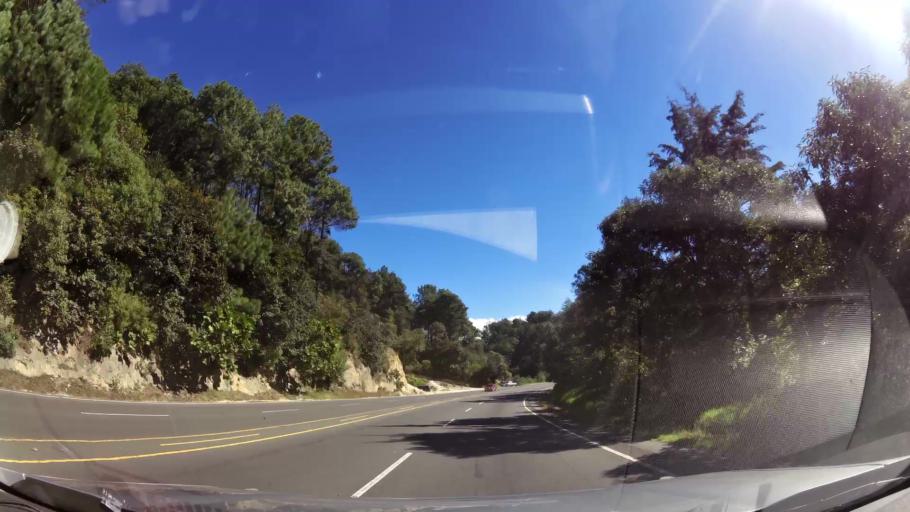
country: GT
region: Solola
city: San Jose Chacaya
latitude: 14.8147
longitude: -91.2079
